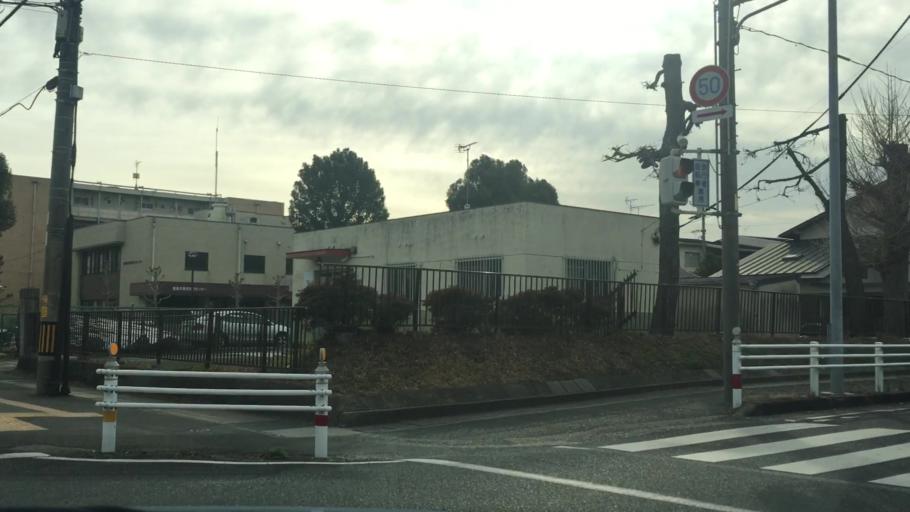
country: JP
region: Aichi
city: Toyohashi
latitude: 34.7427
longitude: 137.3855
